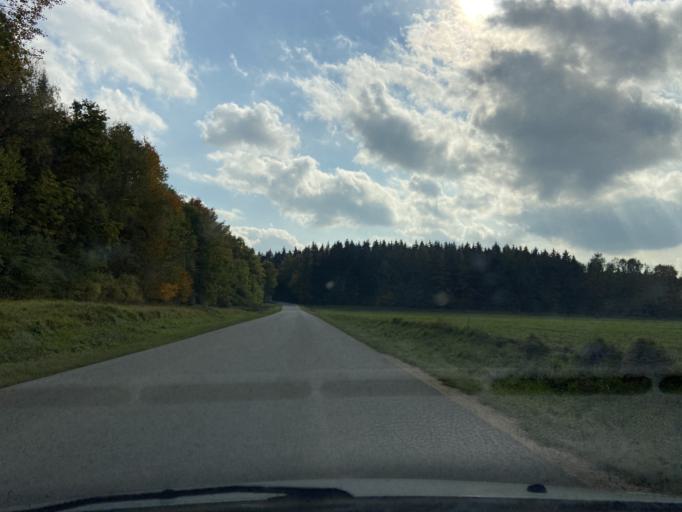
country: DE
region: Baden-Wuerttemberg
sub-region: Tuebingen Region
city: Sigmaringen
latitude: 48.0718
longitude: 9.2238
